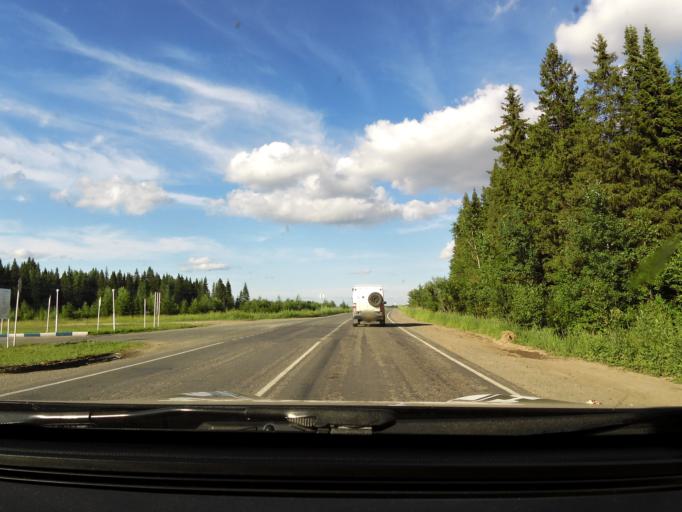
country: RU
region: Kirov
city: Omutninsk
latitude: 58.6854
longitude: 52.1488
